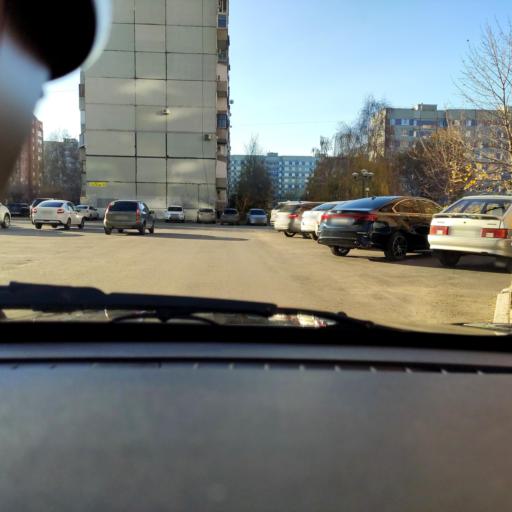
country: RU
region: Samara
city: Tol'yatti
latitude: 53.5415
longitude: 49.3333
